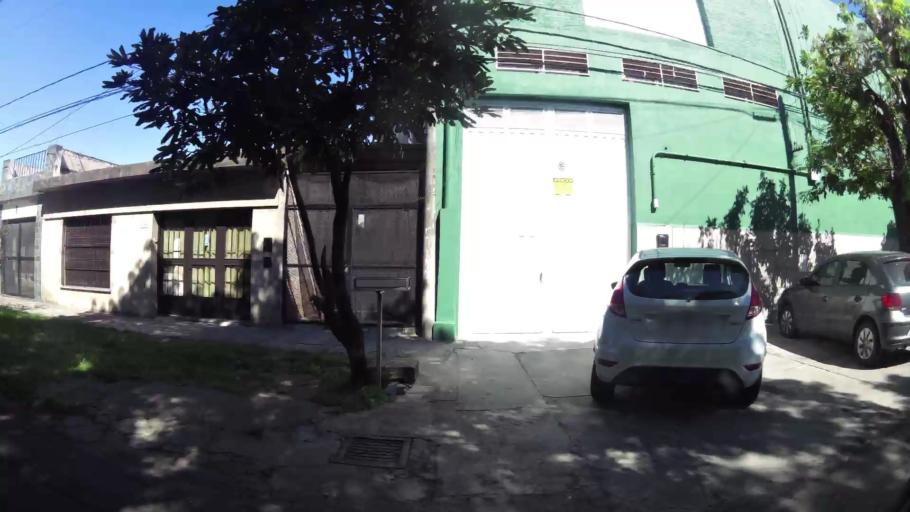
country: AR
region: Santa Fe
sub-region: Departamento de Rosario
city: Rosario
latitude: -32.9545
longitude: -60.6845
